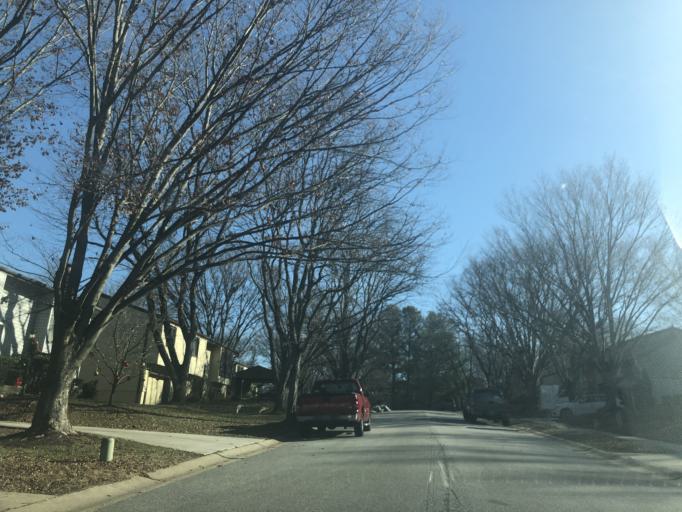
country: US
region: Maryland
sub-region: Howard County
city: Columbia
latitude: 39.1970
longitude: -76.8446
